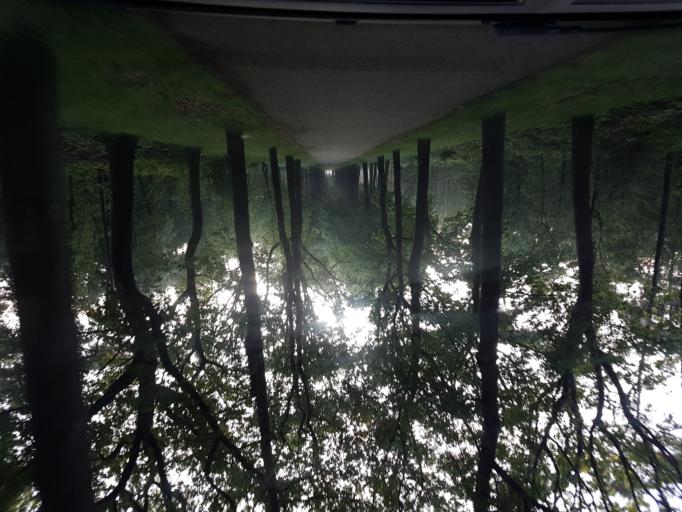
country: BE
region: Flanders
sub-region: Provincie Antwerpen
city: Hoogstraten
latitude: 51.3951
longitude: 4.8136
